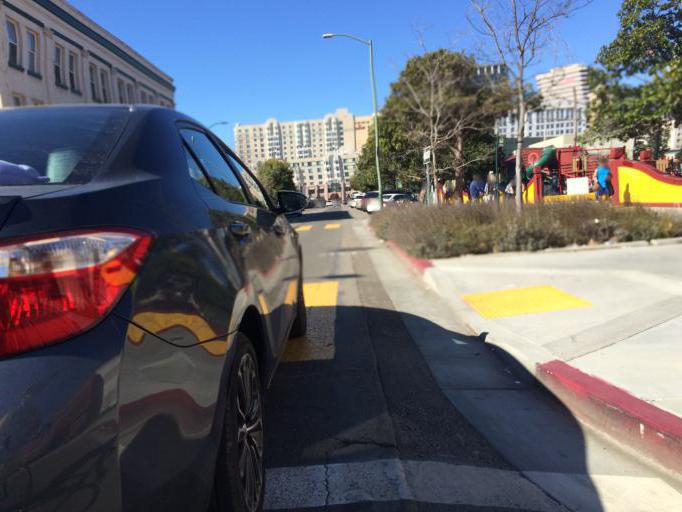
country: US
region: California
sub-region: Alameda County
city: Oakland
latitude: 37.7997
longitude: -122.2681
